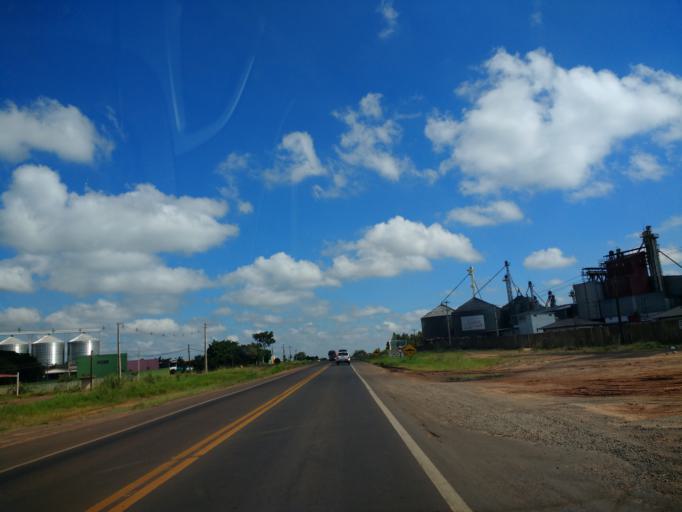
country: BR
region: Parana
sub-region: Umuarama
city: Umuarama
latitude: -23.8106
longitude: -53.3241
